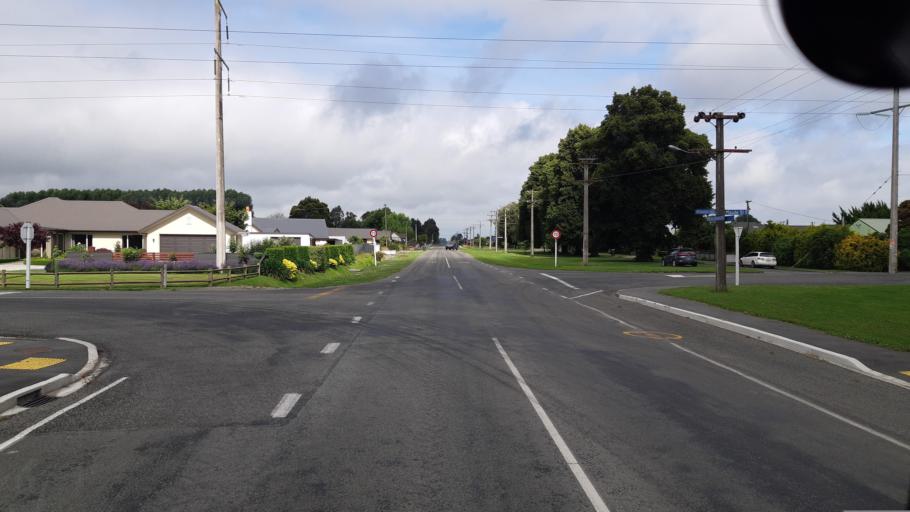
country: NZ
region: Canterbury
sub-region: Timaru District
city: Pleasant Point
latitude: -44.2406
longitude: 171.2951
